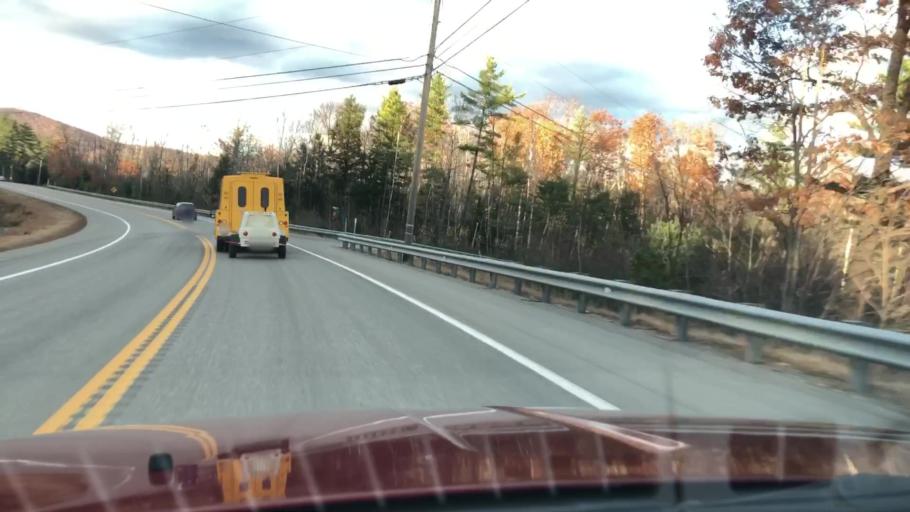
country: US
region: Maine
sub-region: Oxford County
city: Peru
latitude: 44.5308
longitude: -70.4056
